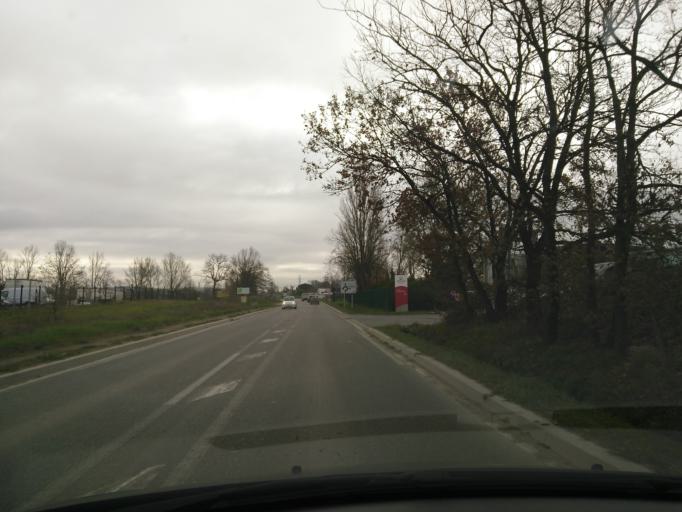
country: FR
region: Midi-Pyrenees
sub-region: Departement de la Haute-Garonne
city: Pinsaguel
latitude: 43.5302
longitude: 1.3706
